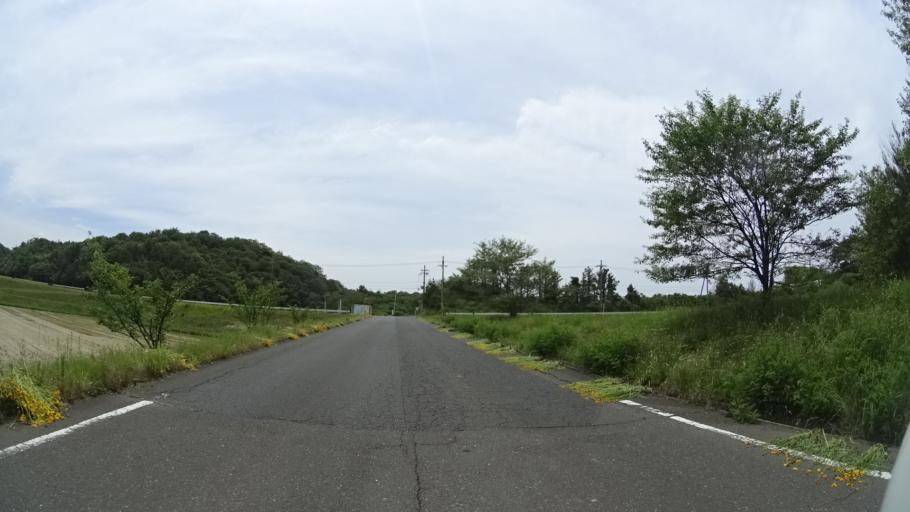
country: JP
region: Kyoto
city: Miyazu
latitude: 35.6795
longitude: 135.0660
